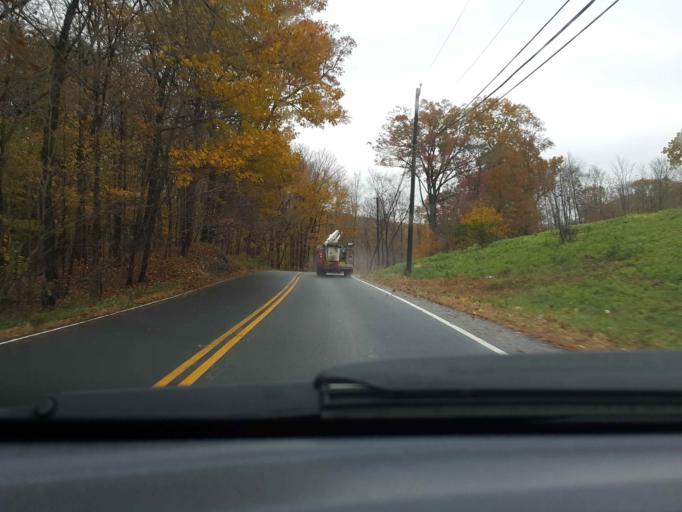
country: US
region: Connecticut
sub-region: Middlesex County
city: Durham
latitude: 41.4263
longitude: -72.6920
